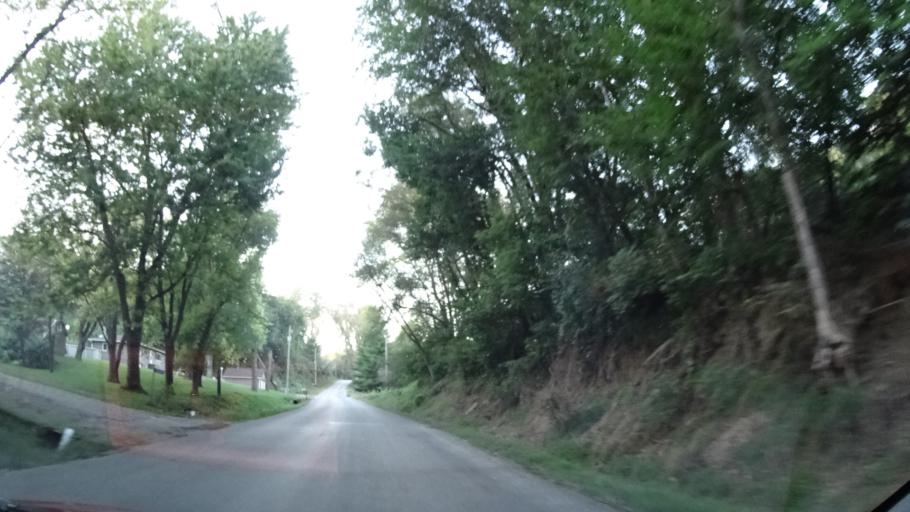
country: US
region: Iowa
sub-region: Pottawattamie County
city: Council Bluffs
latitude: 41.2956
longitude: -95.8561
